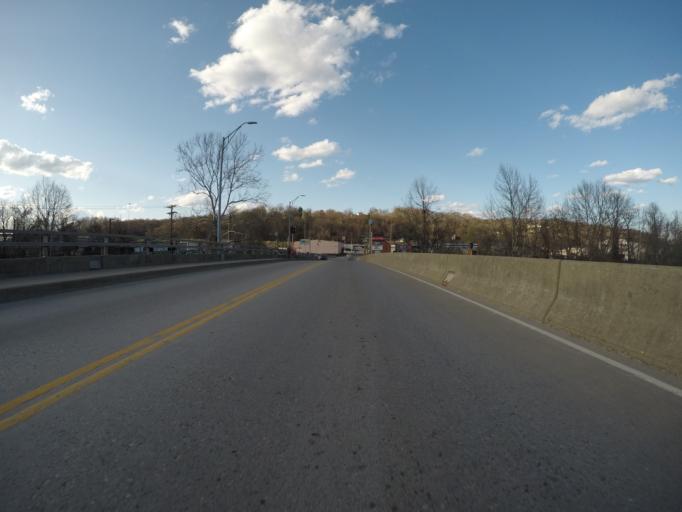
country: US
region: West Virginia
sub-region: Kanawha County
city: Charleston
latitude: 38.3583
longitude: -81.6275
